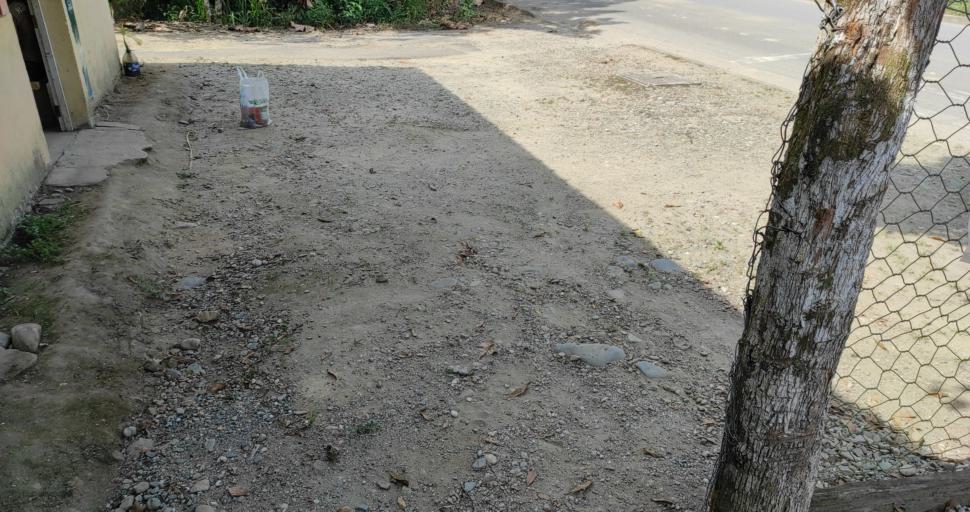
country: EC
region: Zamora-Chinchipe
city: Yantzaza
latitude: -3.7862
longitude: -78.9016
